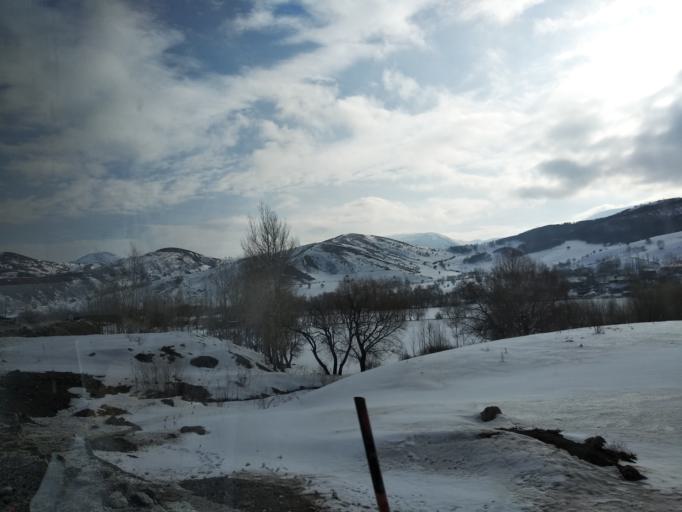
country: TR
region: Erzincan
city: Catalarmut
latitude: 39.9060
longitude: 39.3996
